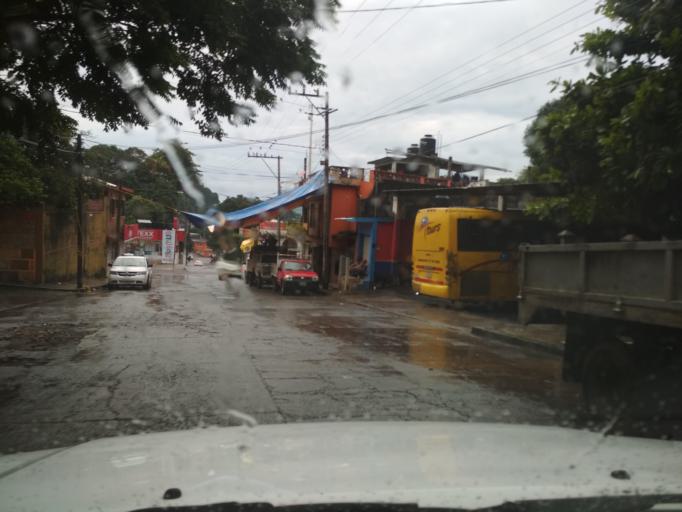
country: MX
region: Veracruz
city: San Andres Tuxtla
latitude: 18.4476
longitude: -95.2027
